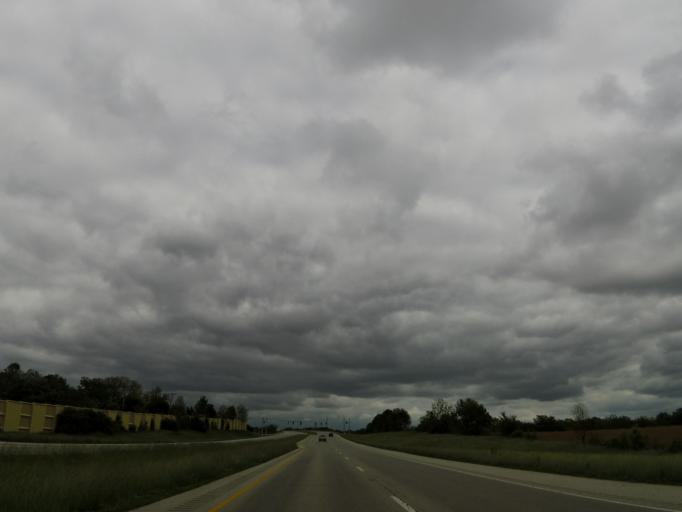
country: US
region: Kentucky
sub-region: Scott County
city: Georgetown
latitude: 38.1854
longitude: -84.5515
